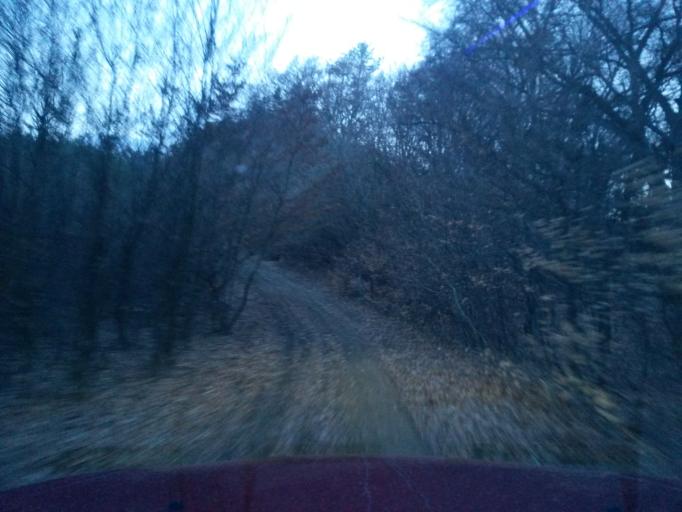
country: SK
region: Kosicky
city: Kosice
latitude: 48.6943
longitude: 21.3814
